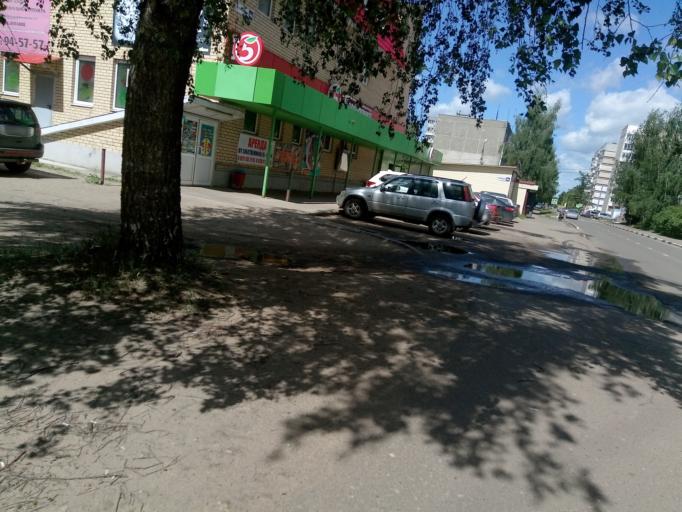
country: RU
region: Jaroslavl
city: Yaroslavl
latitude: 57.6543
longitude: 39.9603
